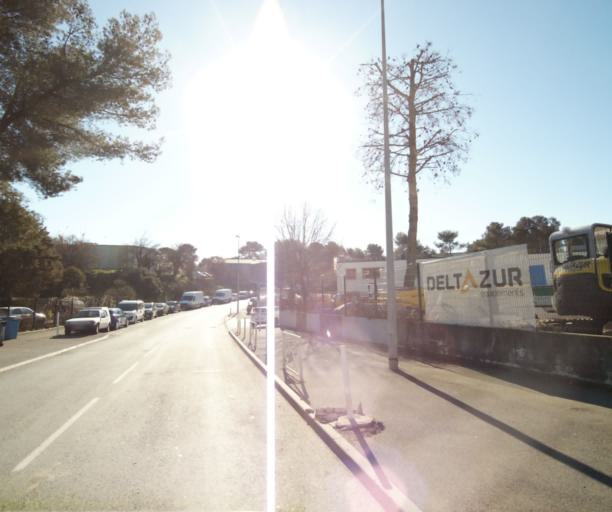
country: FR
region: Provence-Alpes-Cote d'Azur
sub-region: Departement des Alpes-Maritimes
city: Biot
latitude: 43.6050
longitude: 7.0766
